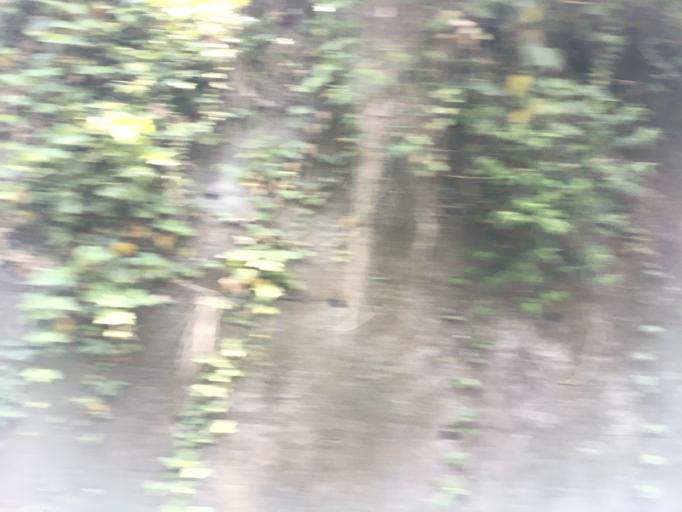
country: TW
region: Taiwan
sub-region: Yilan
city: Yilan
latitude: 24.8173
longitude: 121.7344
